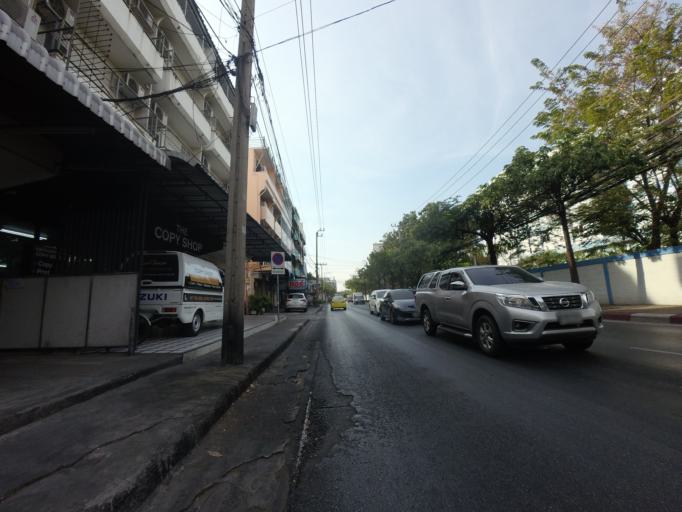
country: TH
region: Bangkok
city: Bang Kapi
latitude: 13.7524
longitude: 100.6170
